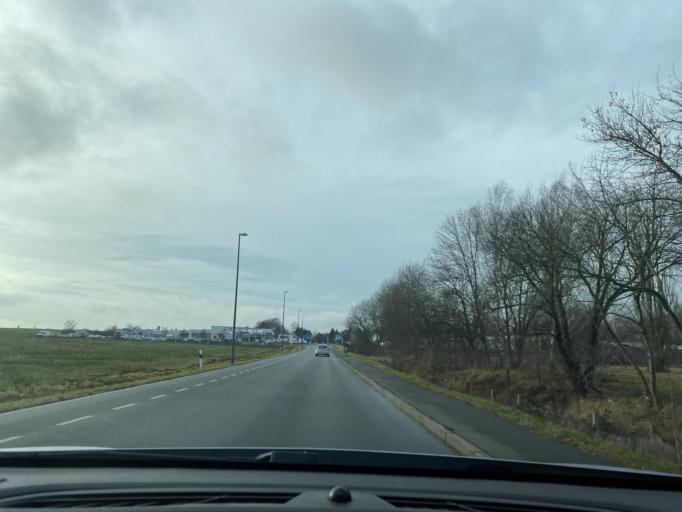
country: DE
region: Saxony
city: Markersdorf
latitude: 51.1472
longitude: 14.9325
